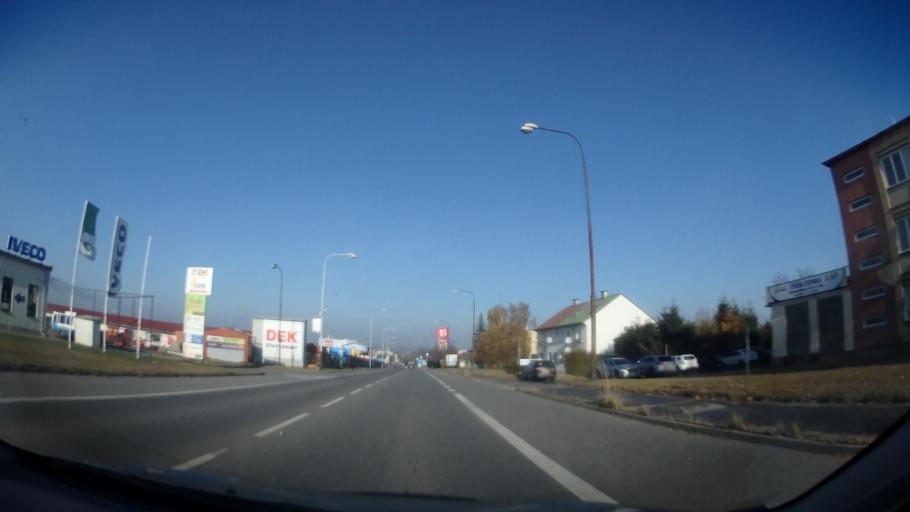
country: CZ
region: Vysocina
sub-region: Okres Zd'ar nad Sazavou
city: Zd'ar nad Sazavou
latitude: 49.5537
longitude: 15.9520
